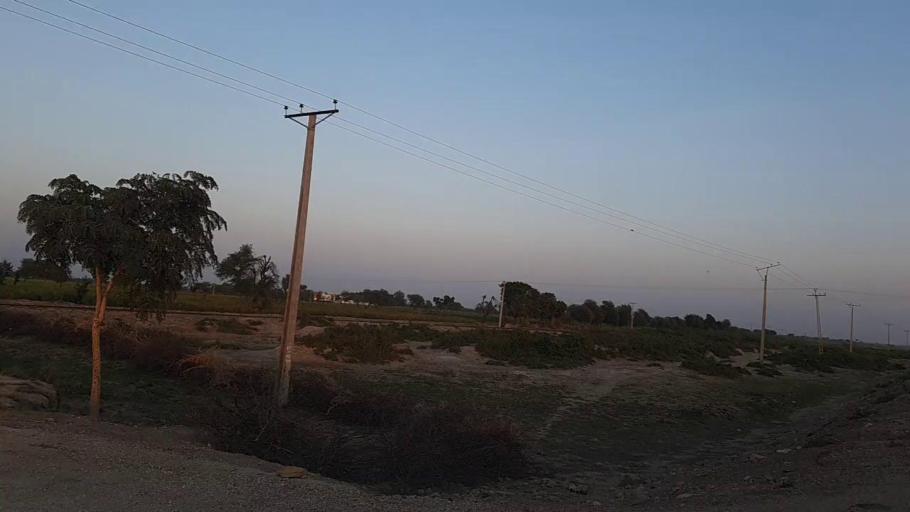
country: PK
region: Sindh
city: Naukot
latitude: 24.8744
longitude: 69.3691
